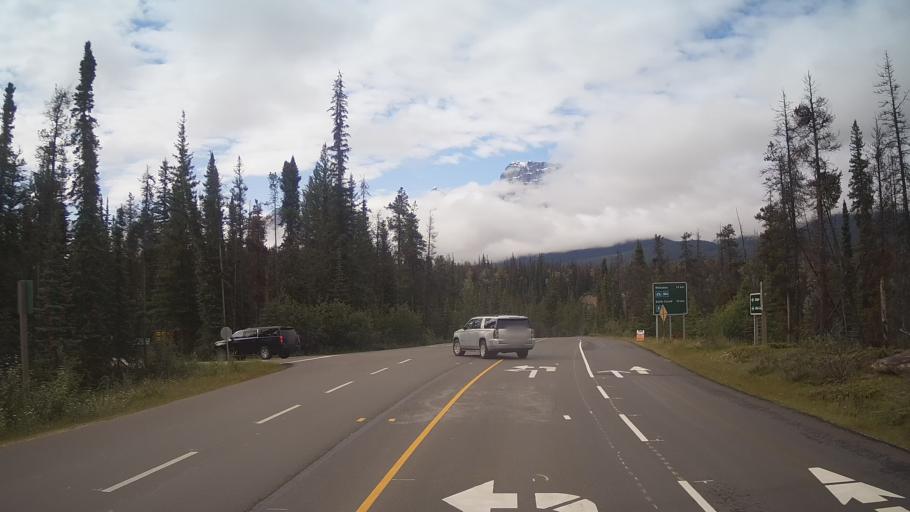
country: CA
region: Alberta
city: Jasper Park Lodge
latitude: 52.6665
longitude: -117.8841
